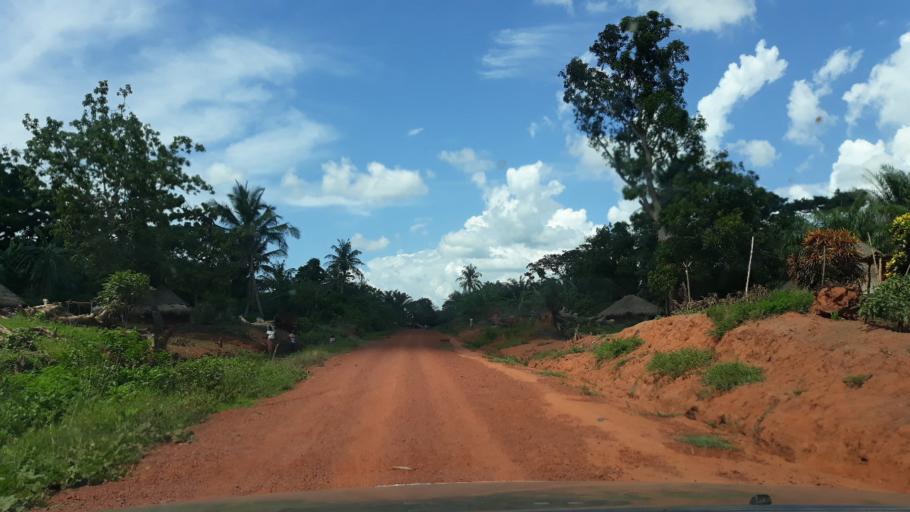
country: CD
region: Equateur
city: Businga
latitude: 3.4088
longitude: 20.3987
